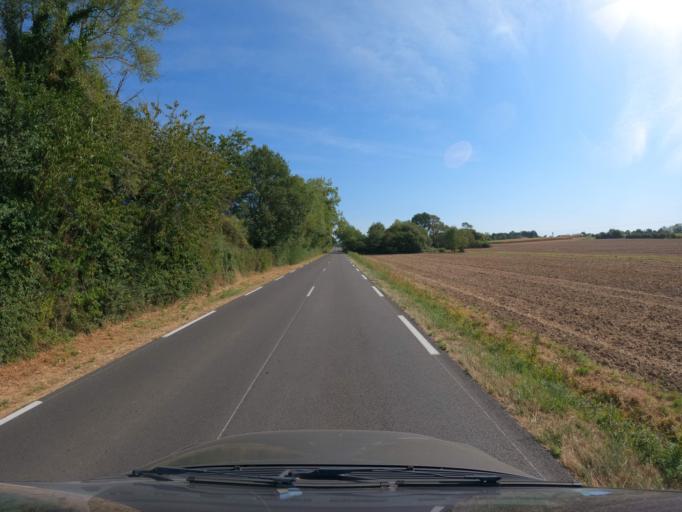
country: FR
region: Pays de la Loire
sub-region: Departement de la Vendee
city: Saint-Christophe-du-Ligneron
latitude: 46.8145
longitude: -1.7706
